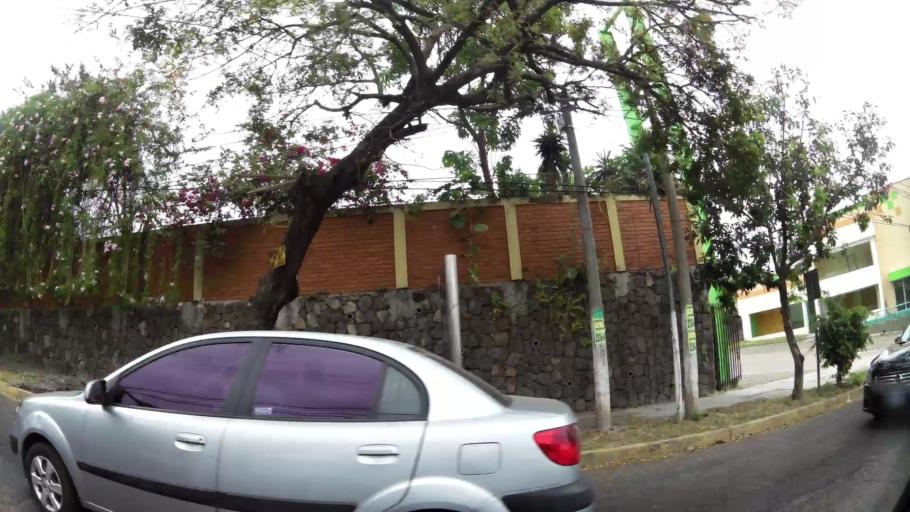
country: SV
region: San Salvador
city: Mejicanos
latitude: 13.7116
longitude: -89.2473
